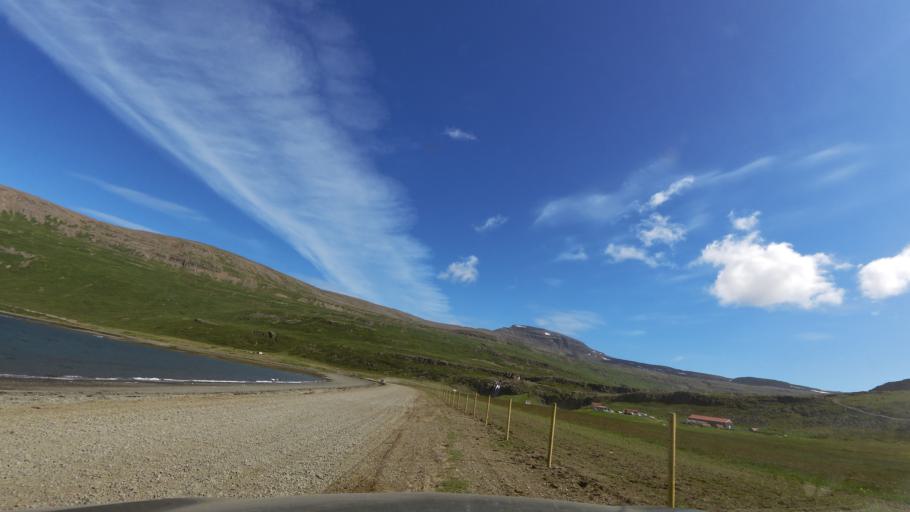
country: IS
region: Westfjords
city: Isafjoerdur
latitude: 65.6044
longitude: -23.5507
